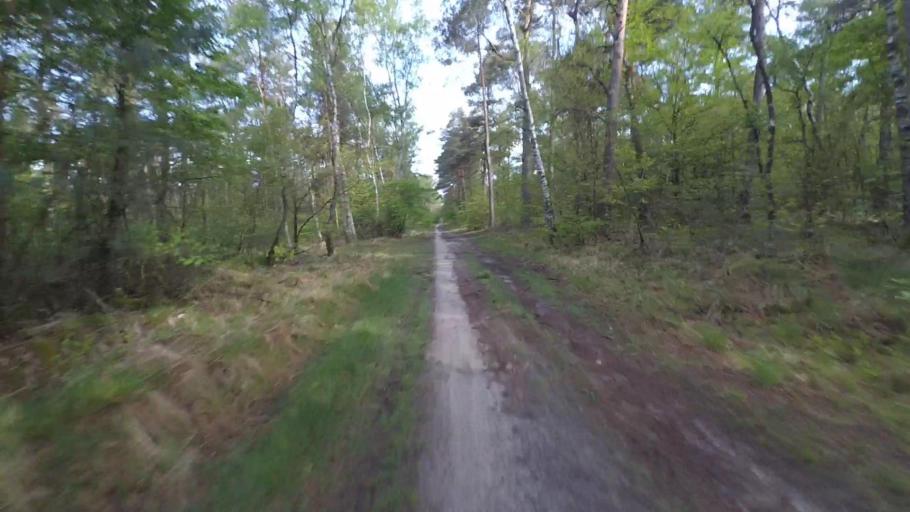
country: NL
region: Utrecht
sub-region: Gemeente Utrechtse Heuvelrug
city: Driebergen-Rijsenburg
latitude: 52.1012
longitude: 5.3150
